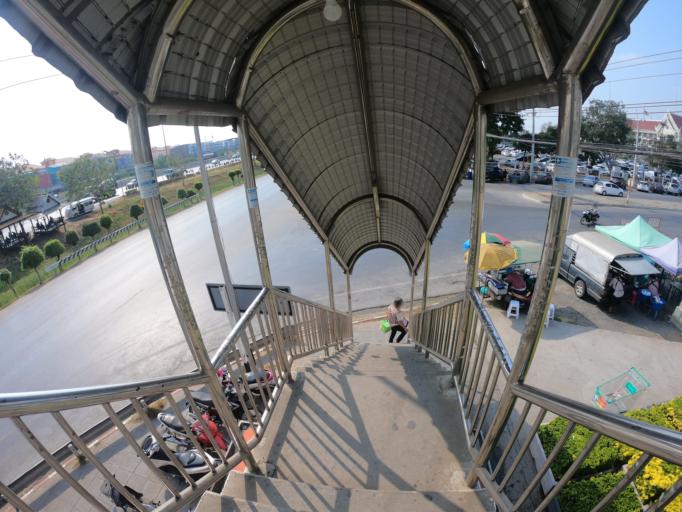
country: TH
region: Phra Nakhon Si Ayutthaya
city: Phra Nakhon Si Ayutthaya
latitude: 14.3532
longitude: 100.6031
